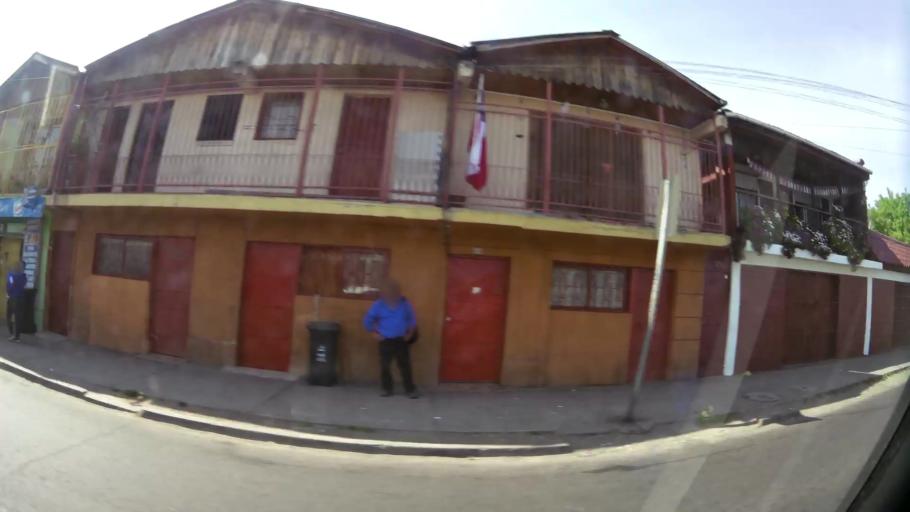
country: CL
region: Santiago Metropolitan
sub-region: Provincia de Santiago
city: Lo Prado
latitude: -33.4368
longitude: -70.7675
